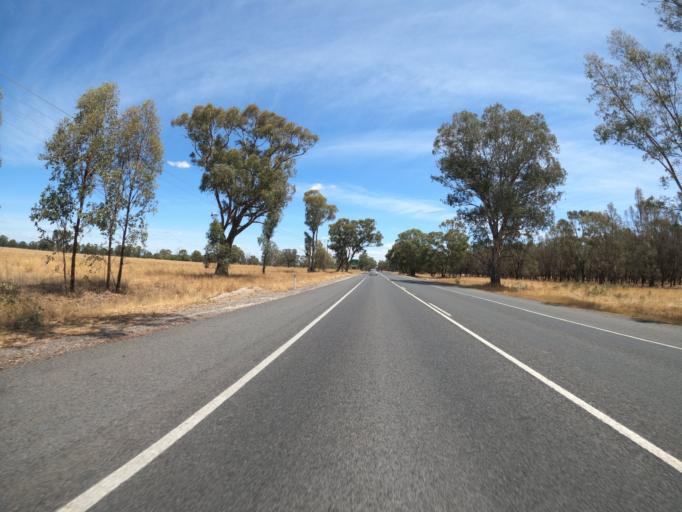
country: AU
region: Victoria
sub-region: Benalla
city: Benalla
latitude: -36.5288
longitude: 146.0442
